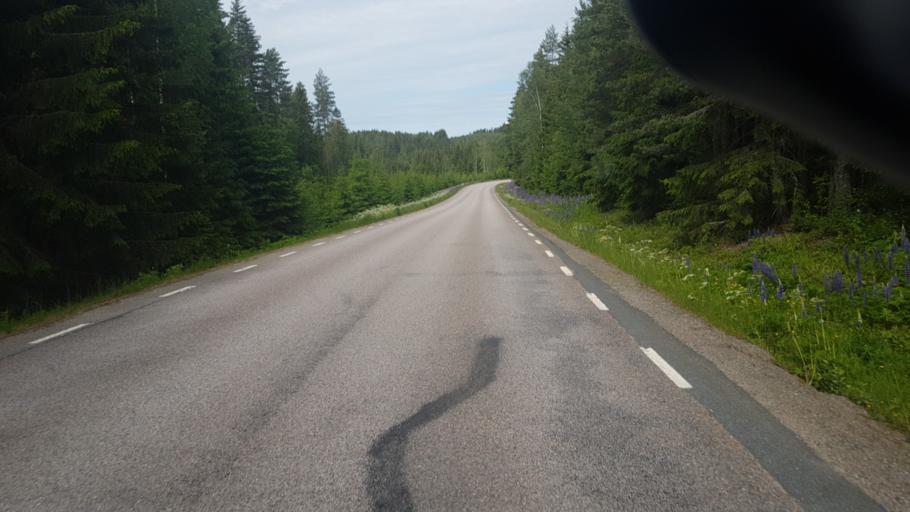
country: SE
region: Vaermland
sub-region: Eda Kommun
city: Charlottenberg
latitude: 59.8784
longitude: 12.3777
